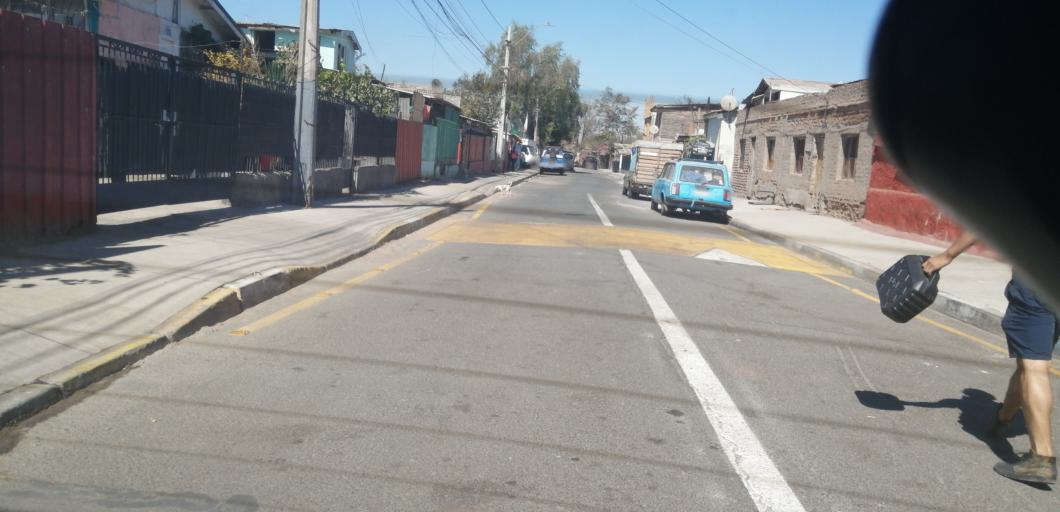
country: CL
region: Santiago Metropolitan
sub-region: Provincia de Santiago
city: Lo Prado
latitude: -33.4396
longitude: -70.7665
